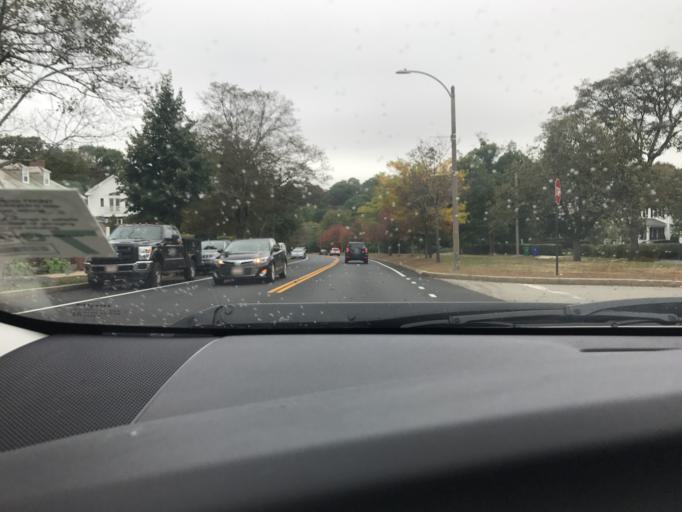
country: US
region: Massachusetts
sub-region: Middlesex County
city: Newton
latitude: 42.3381
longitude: -71.2033
